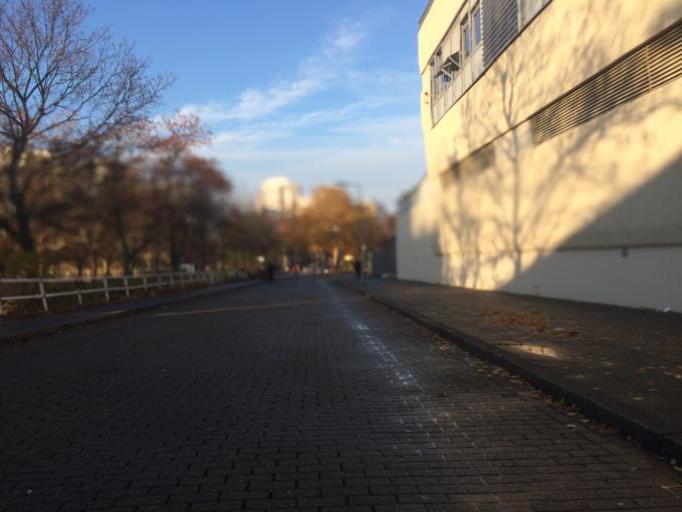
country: DE
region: Berlin
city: Markisches Viertel
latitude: 52.5991
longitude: 13.3535
